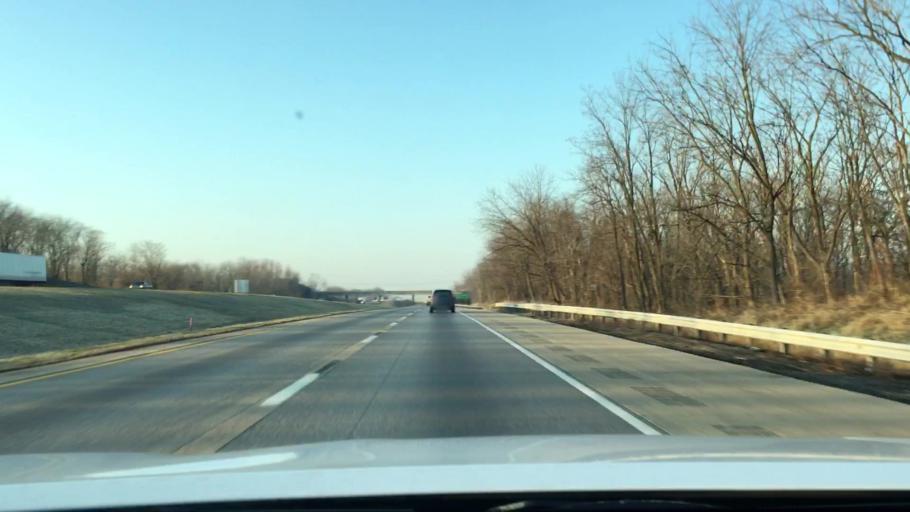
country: US
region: Pennsylvania
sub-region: Lebanon County
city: Palmyra
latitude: 40.4100
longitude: -76.5957
